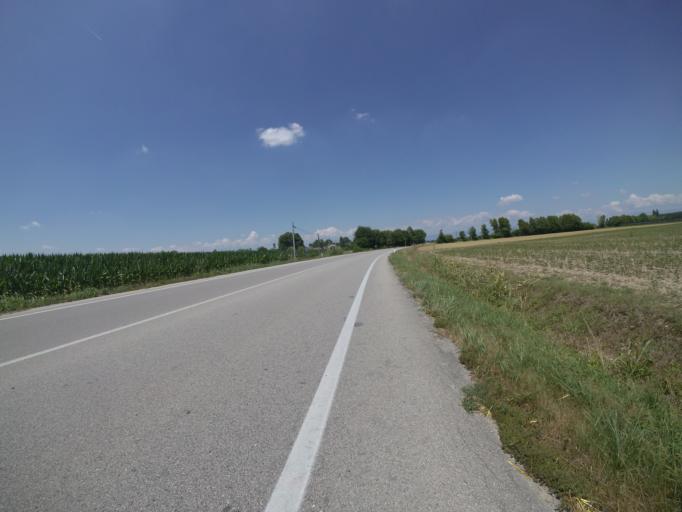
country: IT
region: Friuli Venezia Giulia
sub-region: Provincia di Udine
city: Varmo
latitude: 45.9155
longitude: 12.9963
